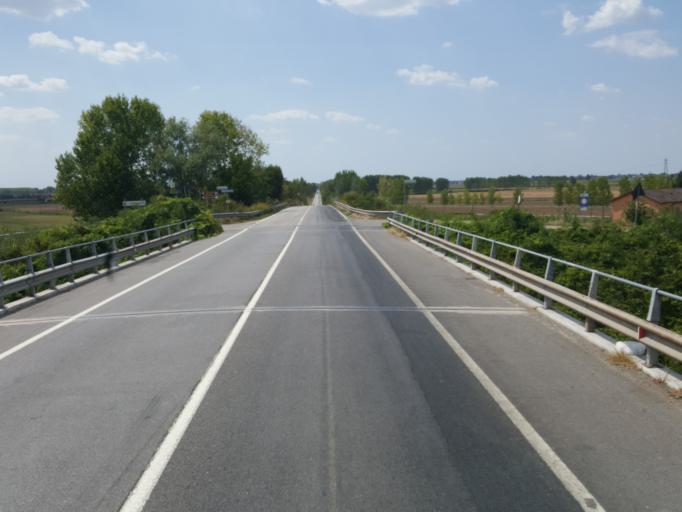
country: IT
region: Lombardy
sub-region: Provincia di Mantova
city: San Benedetto Po
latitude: 45.0909
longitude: 10.9486
